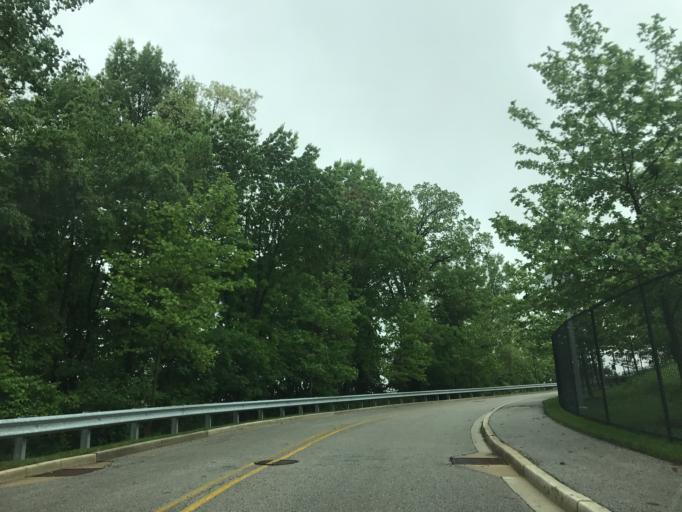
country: US
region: Maryland
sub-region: City of Baltimore
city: Baltimore
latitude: 39.3402
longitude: -76.6516
